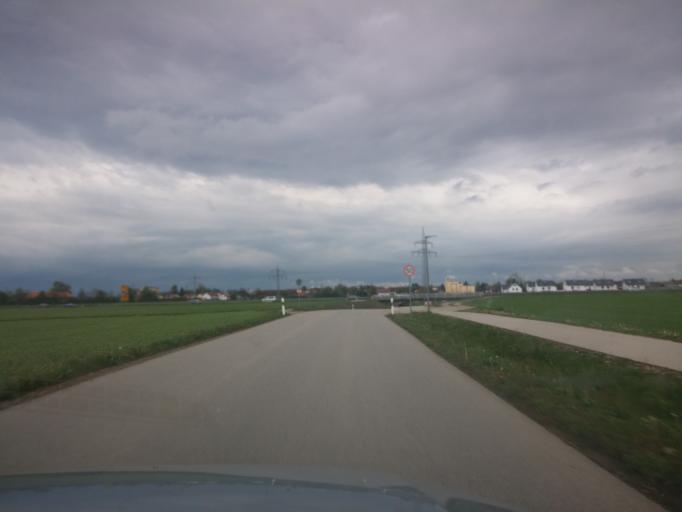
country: DE
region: Bavaria
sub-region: Upper Bavaria
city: Putzbrunn
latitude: 48.0848
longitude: 11.7134
